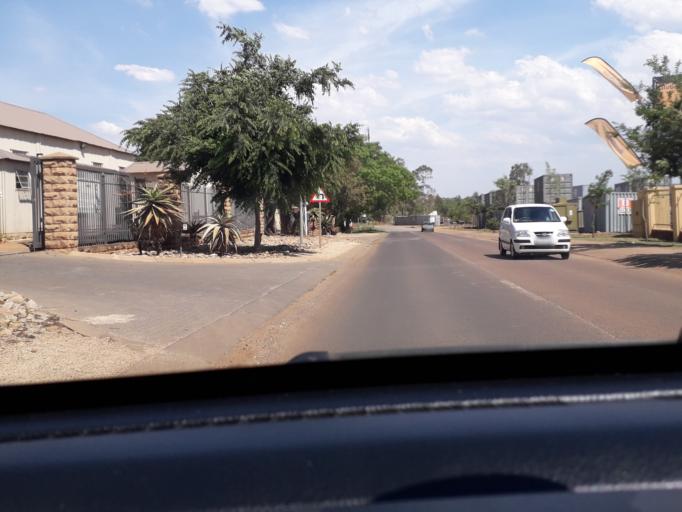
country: ZA
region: Gauteng
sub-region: City of Tshwane Metropolitan Municipality
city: Centurion
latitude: -25.8473
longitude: 28.2216
